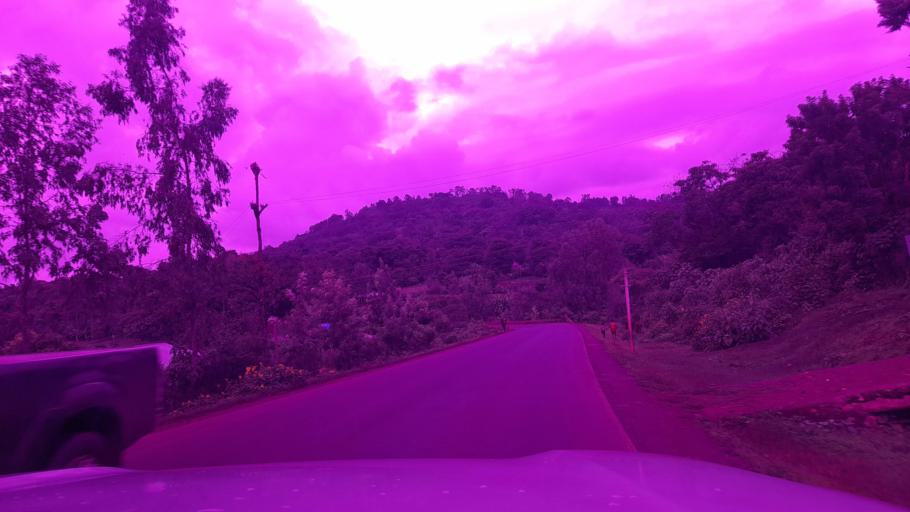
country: ET
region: Oromiya
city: Jima
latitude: 7.9004
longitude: 37.3888
